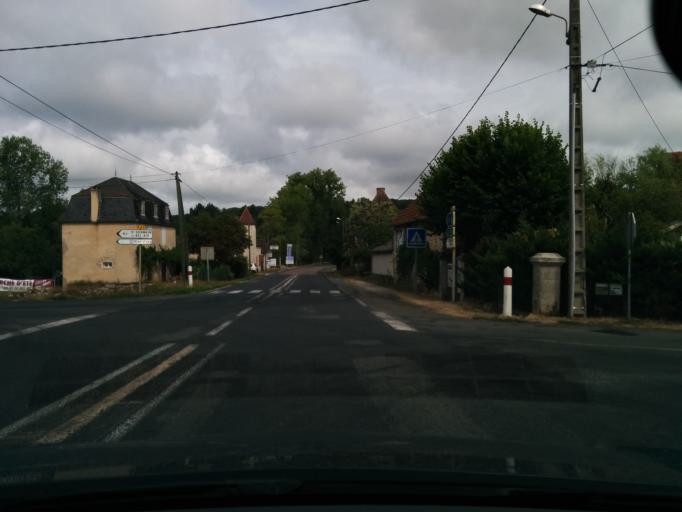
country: FR
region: Midi-Pyrenees
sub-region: Departement du Lot
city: Le Vigan
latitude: 44.6716
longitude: 1.4781
